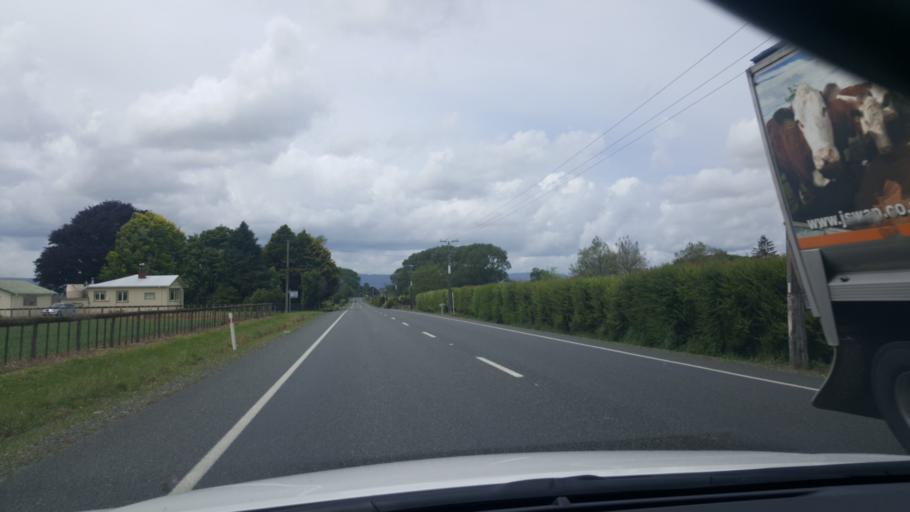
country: NZ
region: Waikato
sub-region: Matamata-Piako District
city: Matamata
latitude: -37.8813
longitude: 175.7431
